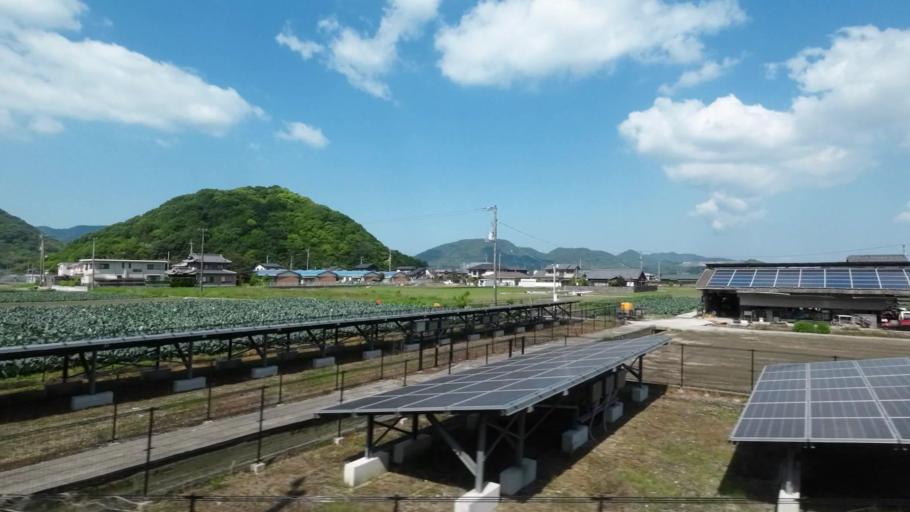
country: JP
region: Kagawa
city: Tadotsu
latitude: 34.1969
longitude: 133.7130
